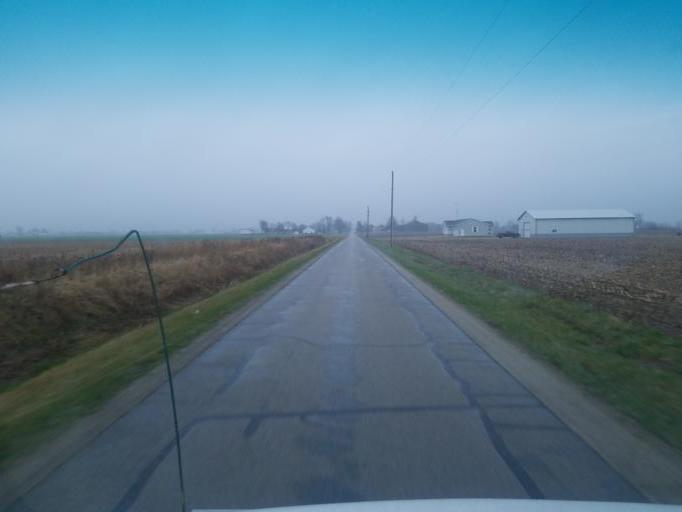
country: US
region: Ohio
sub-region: Henry County
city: Napoleon
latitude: 41.4133
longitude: -84.2160
